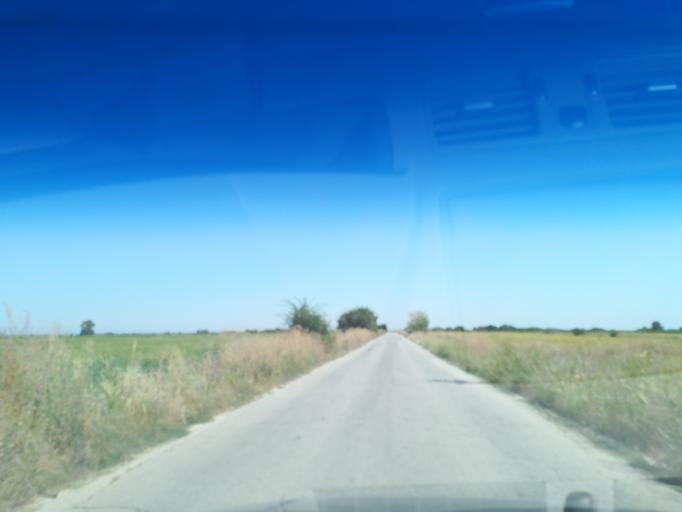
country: BG
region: Plovdiv
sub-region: Obshtina Suedinenie
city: Suedinenie
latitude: 42.2511
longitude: 24.4823
